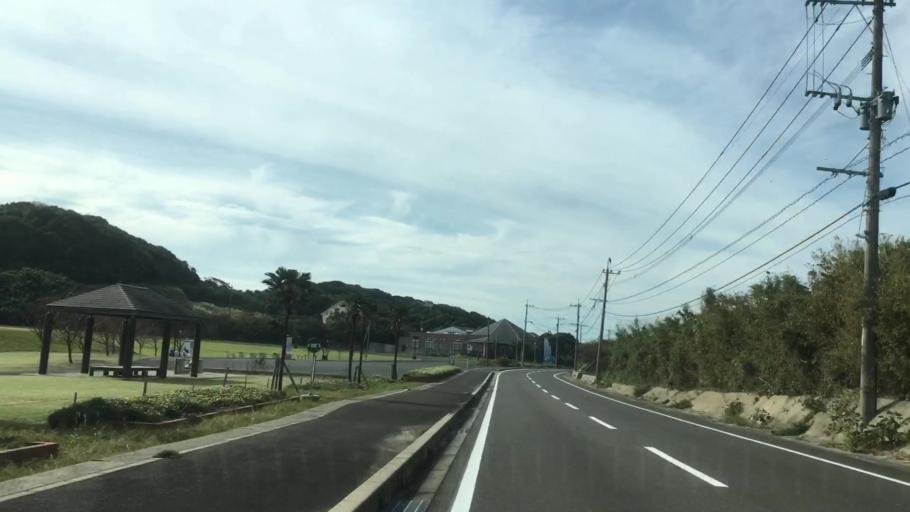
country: JP
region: Nagasaki
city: Sasebo
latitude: 33.0167
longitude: 129.5739
